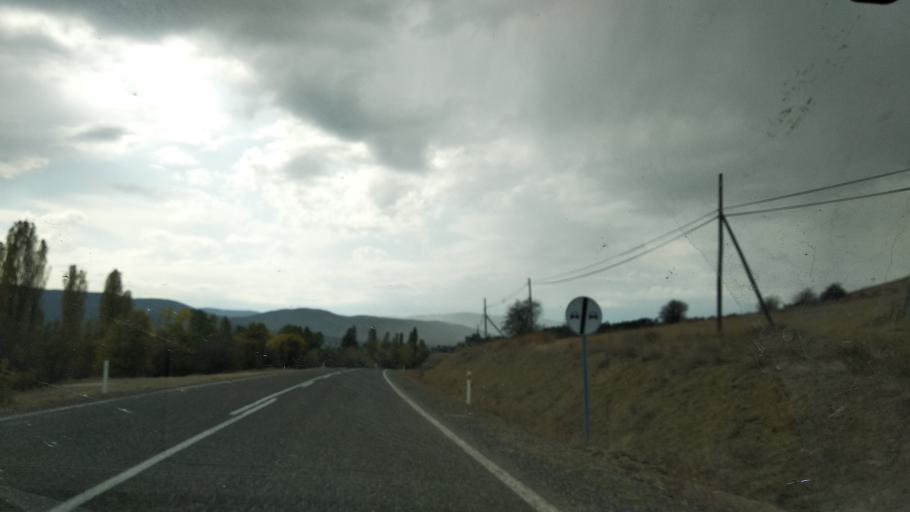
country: TR
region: Bolu
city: Seben
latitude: 40.3404
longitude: 31.4721
